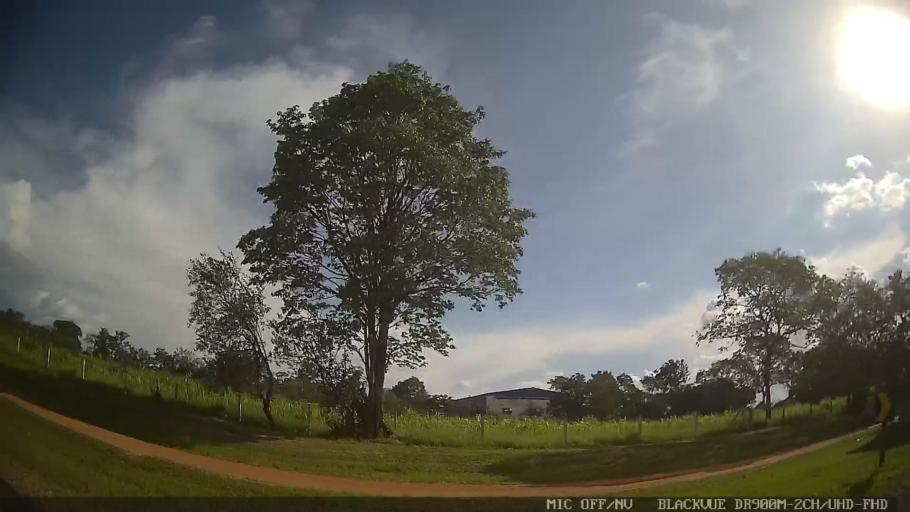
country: BR
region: Sao Paulo
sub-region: Laranjal Paulista
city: Laranjal Paulista
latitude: -23.0788
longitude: -47.7959
